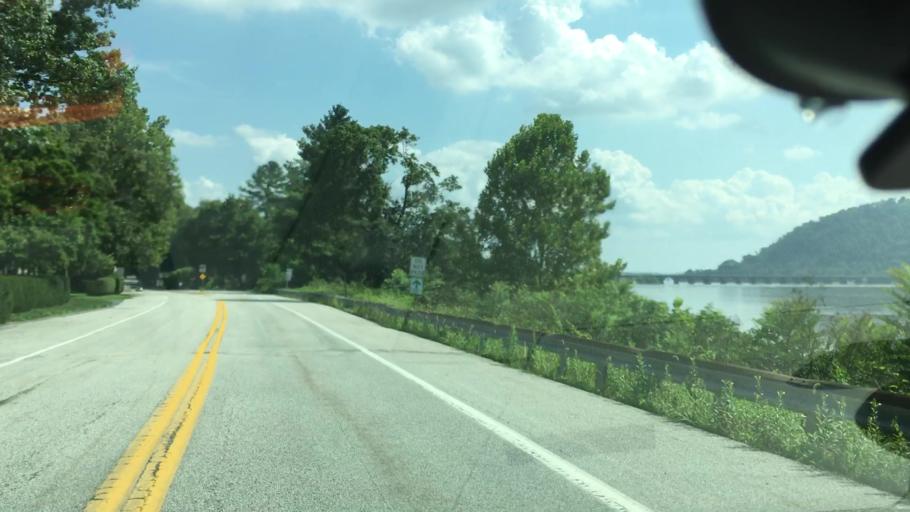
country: US
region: Pennsylvania
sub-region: Perry County
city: Marysville
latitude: 40.3460
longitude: -76.9123
